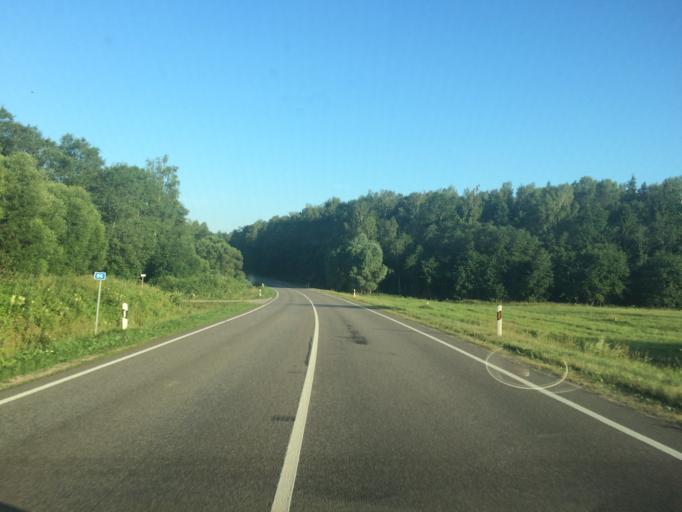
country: LT
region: Utenos apskritis
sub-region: Anyksciai
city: Anyksciai
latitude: 55.4035
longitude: 25.1338
